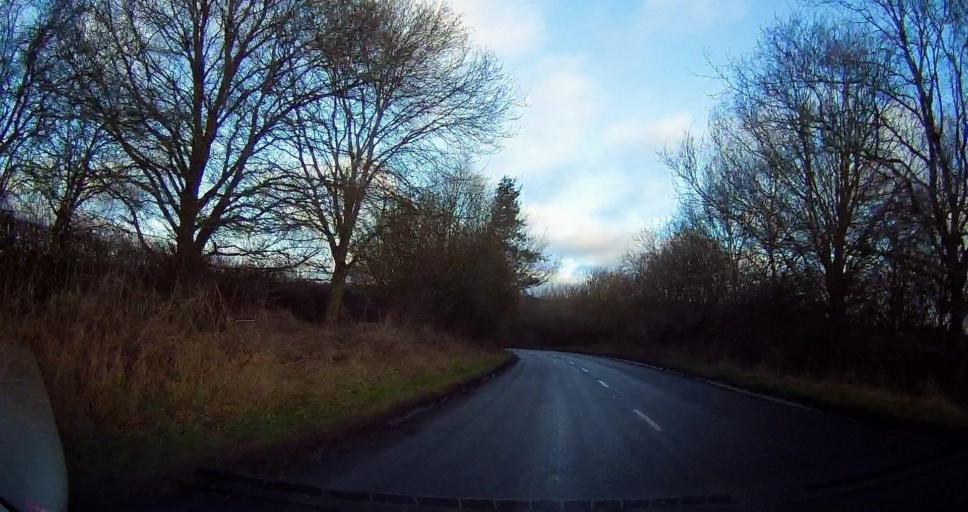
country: GB
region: England
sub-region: Kent
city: Westerham
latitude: 51.2738
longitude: 0.0857
